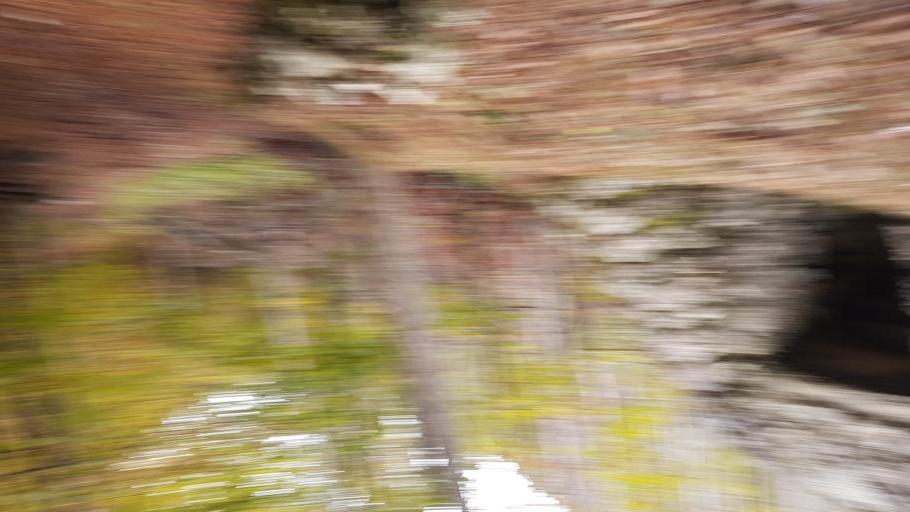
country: IT
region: Friuli Venezia Giulia
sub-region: Provincia di Udine
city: Chiusaforte
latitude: 46.4110
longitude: 13.3402
